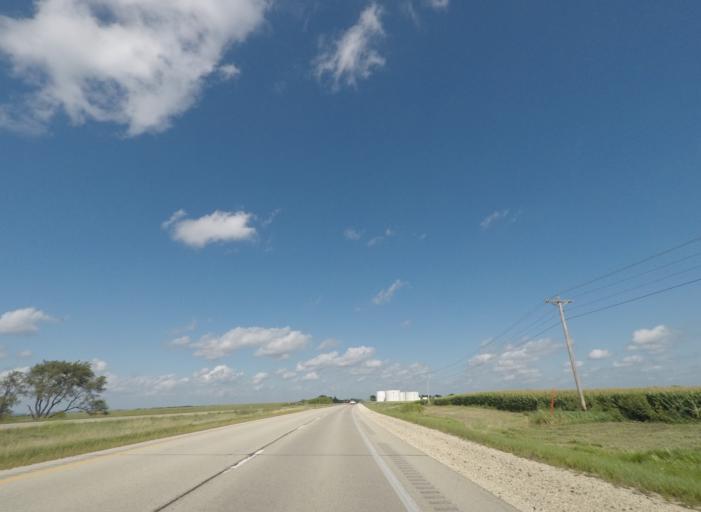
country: US
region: Iowa
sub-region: Dubuque County
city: Asbury
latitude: 42.4098
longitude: -90.7387
